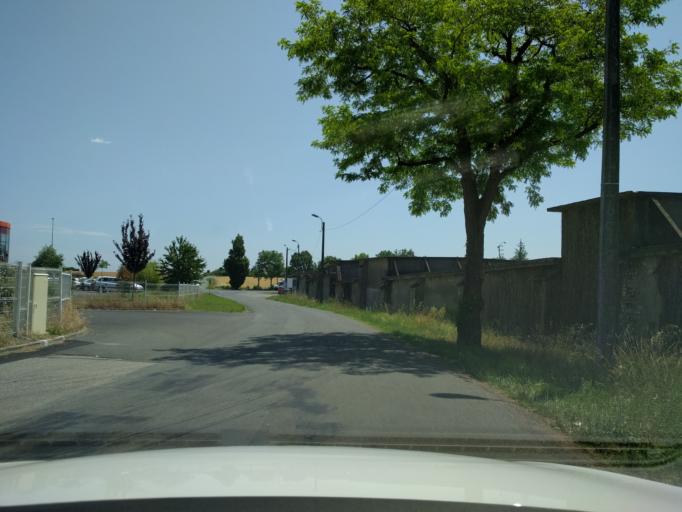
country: FR
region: Poitou-Charentes
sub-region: Departement des Deux-Sevres
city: Niort
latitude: 46.3479
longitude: -0.4438
